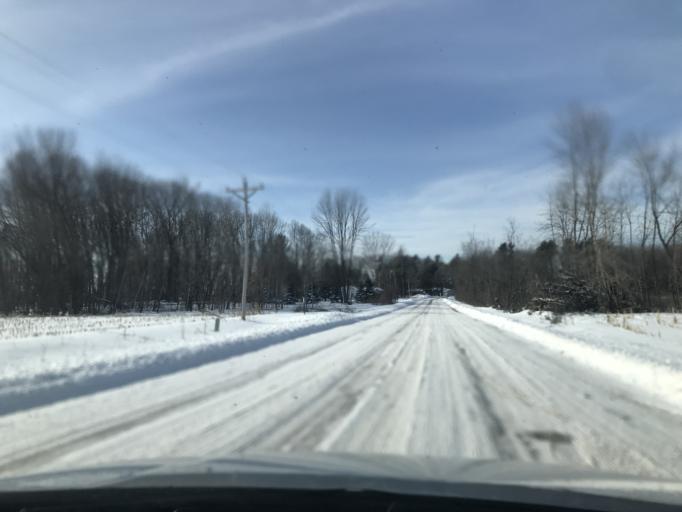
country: US
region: Wisconsin
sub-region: Oconto County
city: Oconto Falls
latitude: 45.1552
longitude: -88.1893
